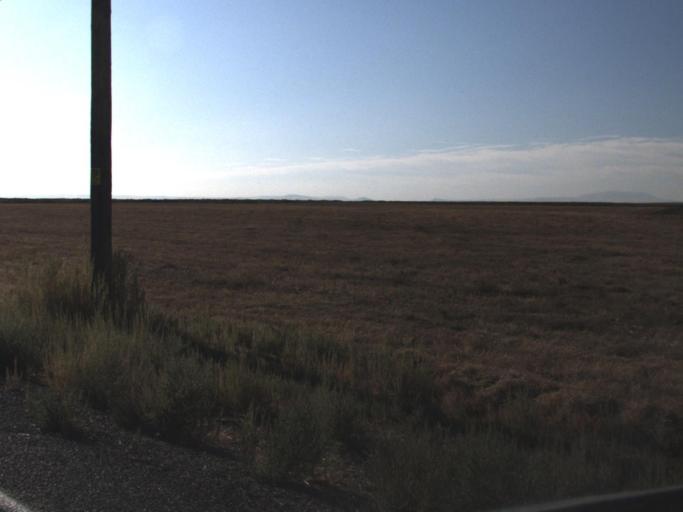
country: US
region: Washington
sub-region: Walla Walla County
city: Burbank
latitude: 46.2439
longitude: -118.8223
